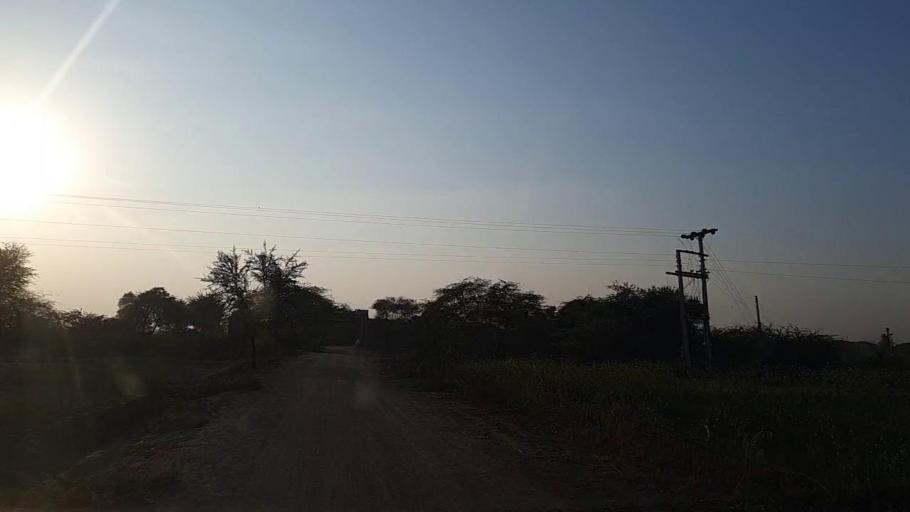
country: PK
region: Sindh
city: Naukot
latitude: 24.9587
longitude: 69.4501
